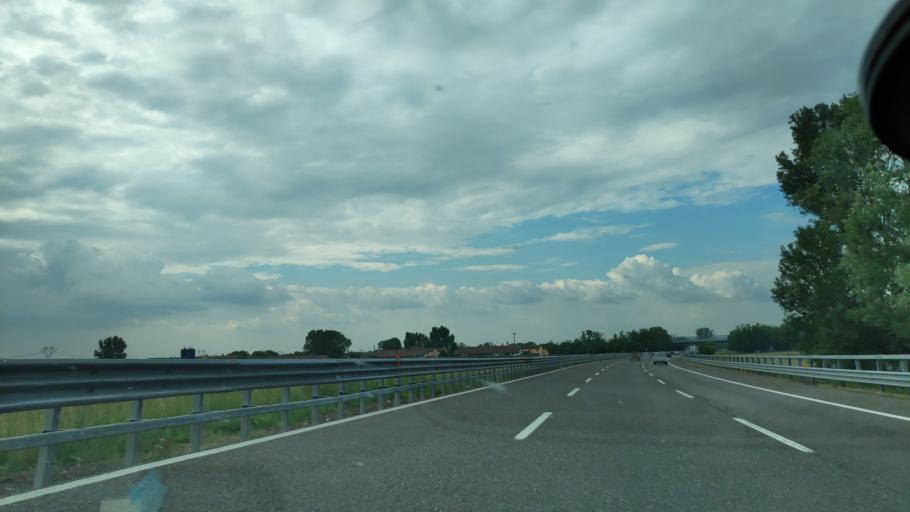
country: IT
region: Lombardy
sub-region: Provincia di Pavia
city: Pieve Albignola
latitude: 45.0913
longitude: 8.9690
